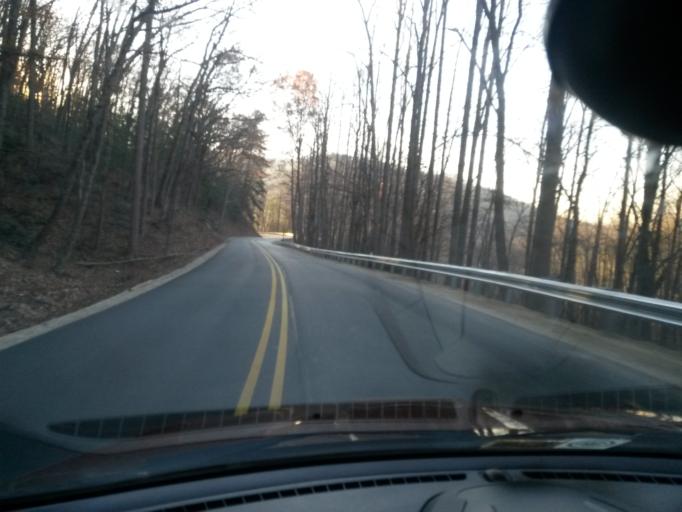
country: US
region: Virginia
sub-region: City of Buena Vista
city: Buena Vista
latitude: 37.7515
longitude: -79.2832
